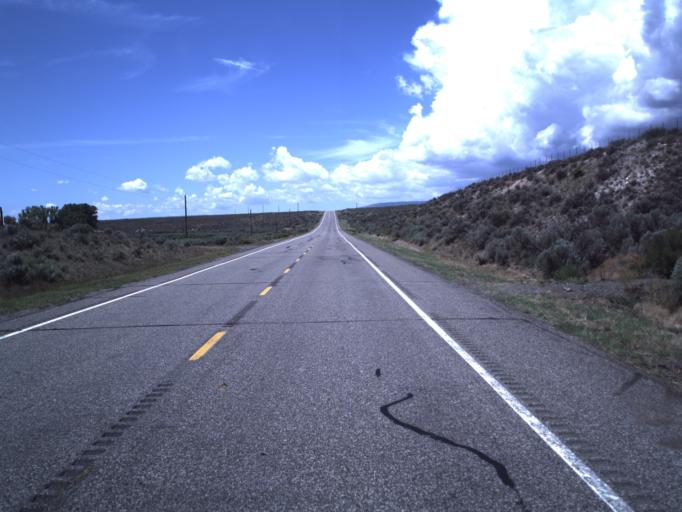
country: US
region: Utah
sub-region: Garfield County
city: Panguitch
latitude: 37.9993
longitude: -112.3858
